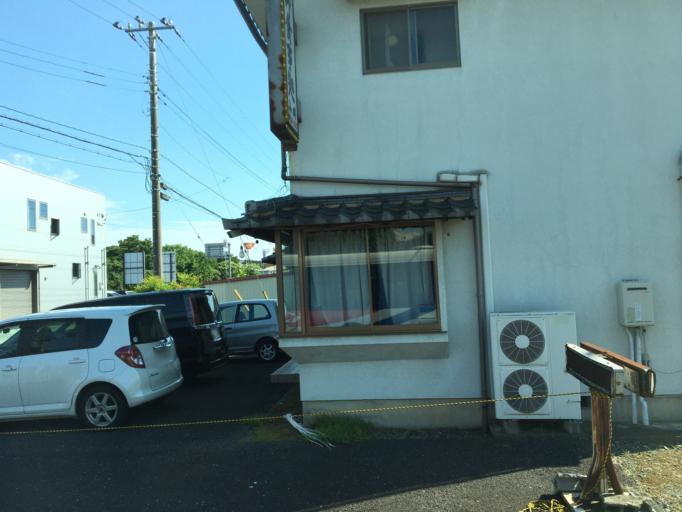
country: JP
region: Saitama
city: Sakado
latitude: 35.9634
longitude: 139.3605
